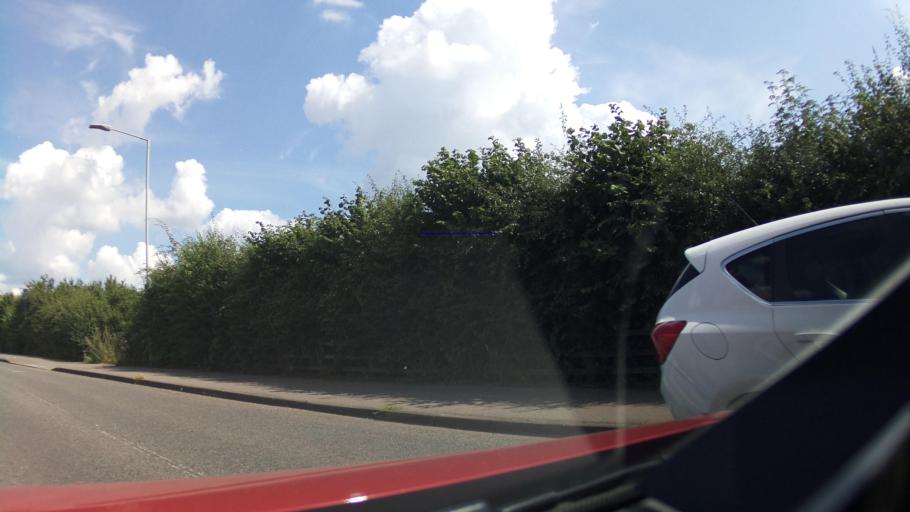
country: GB
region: England
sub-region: West Berkshire
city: Thatcham
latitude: 51.4018
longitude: -1.2716
